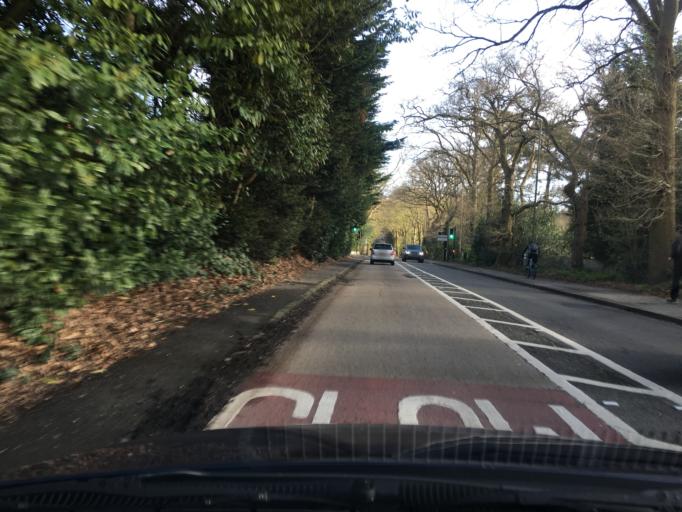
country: GB
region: England
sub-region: Bracknell Forest
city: Sandhurst
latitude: 51.3525
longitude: -0.7991
